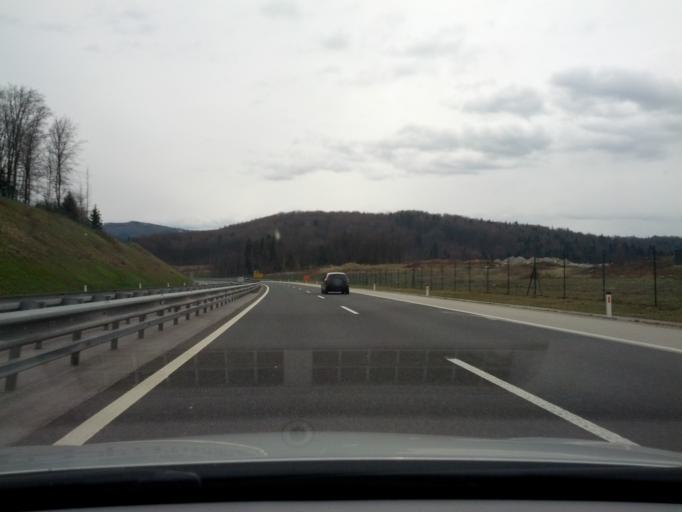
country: SI
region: Mirna Pec
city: Mirna Pec
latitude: 45.8744
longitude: 15.0906
